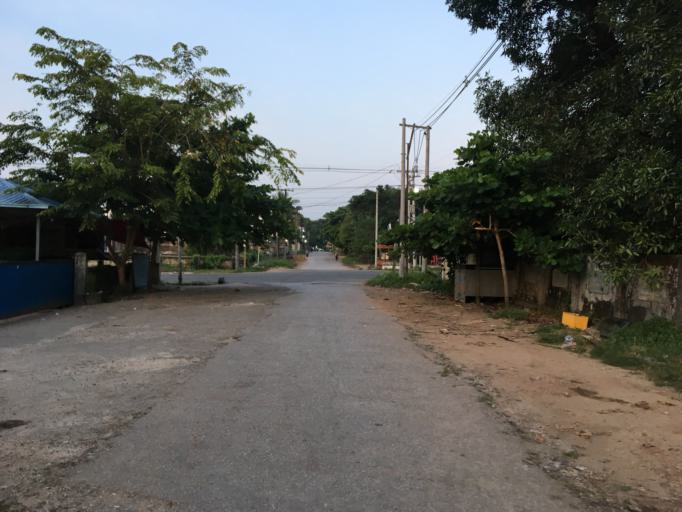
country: MM
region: Mon
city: Mawlamyine
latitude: 16.4790
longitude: 97.6243
